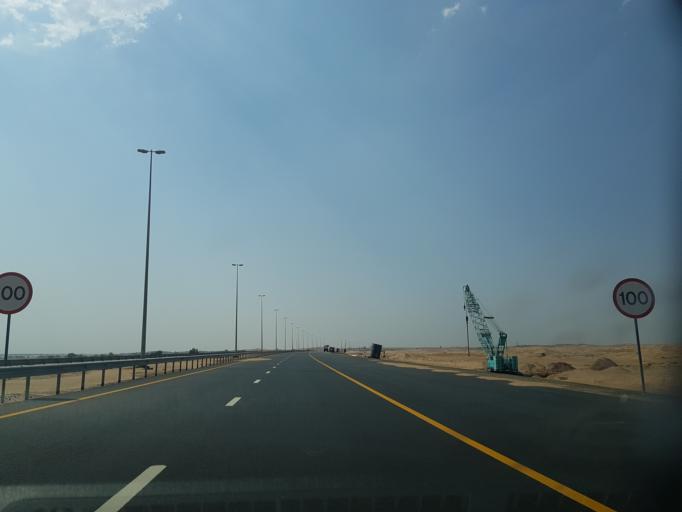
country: AE
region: Ash Shariqah
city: Adh Dhayd
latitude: 25.2601
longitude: 55.6799
